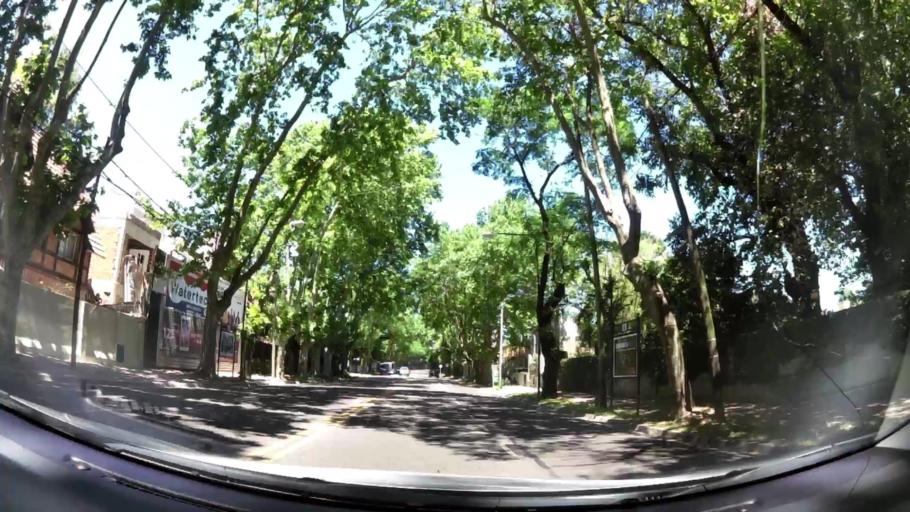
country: AR
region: Buenos Aires
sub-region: Partido de San Isidro
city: San Isidro
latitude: -34.4569
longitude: -58.5222
